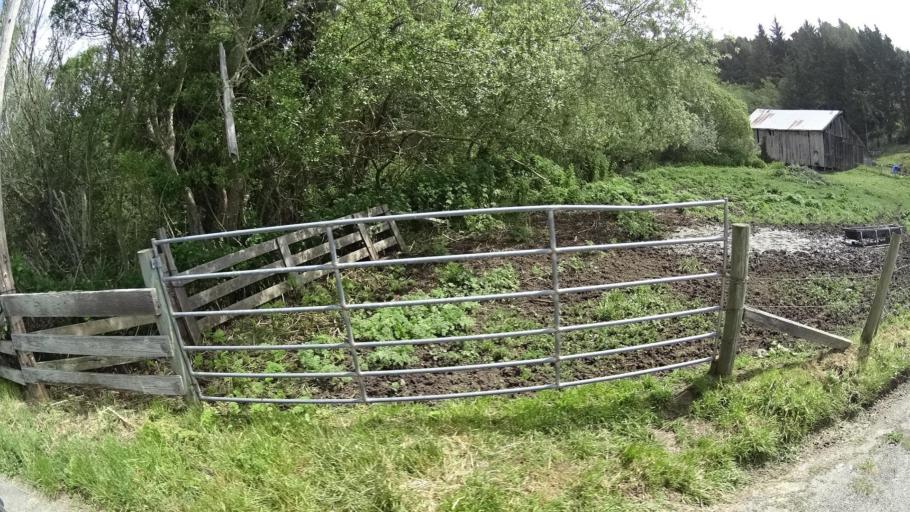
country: US
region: California
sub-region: Humboldt County
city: Humboldt Hill
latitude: 40.6594
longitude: -124.1903
